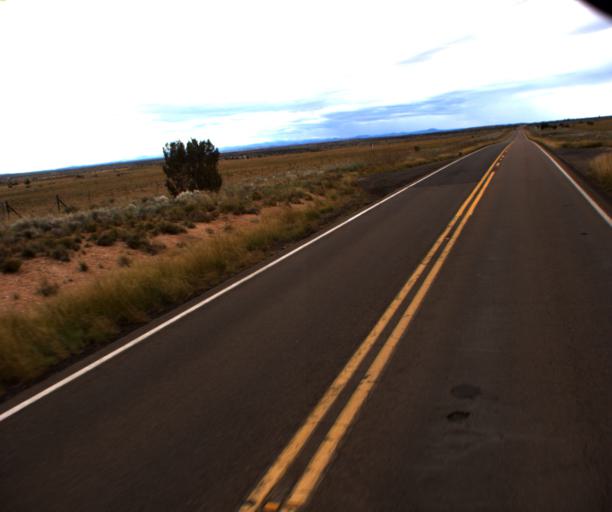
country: US
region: Arizona
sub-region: Navajo County
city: Snowflake
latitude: 34.6060
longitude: -110.0893
